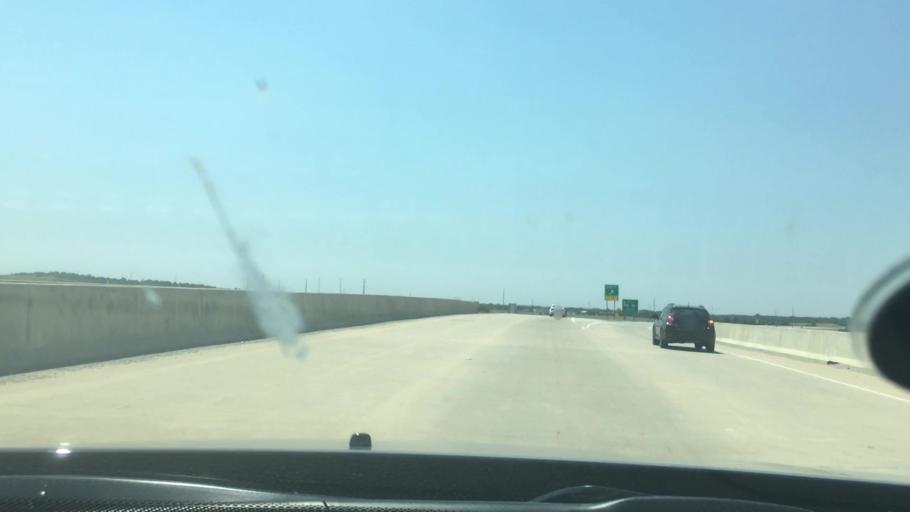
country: US
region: Oklahoma
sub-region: Bryan County
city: Calera
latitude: 33.9671
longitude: -96.4118
